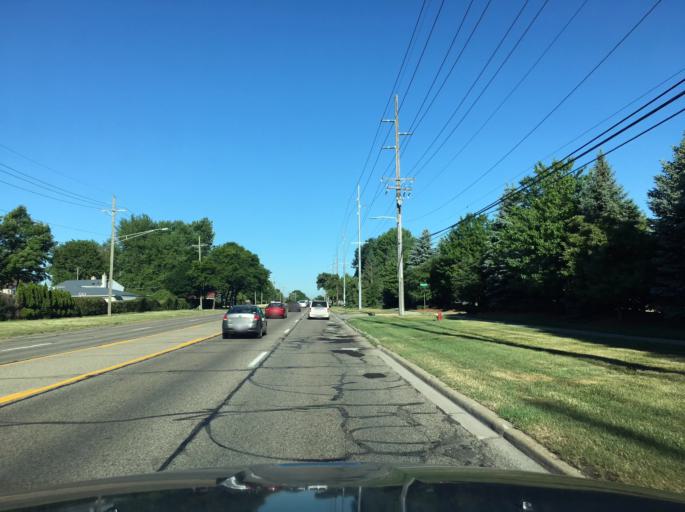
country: US
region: Michigan
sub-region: Macomb County
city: Fraser
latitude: 42.5384
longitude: -82.9720
